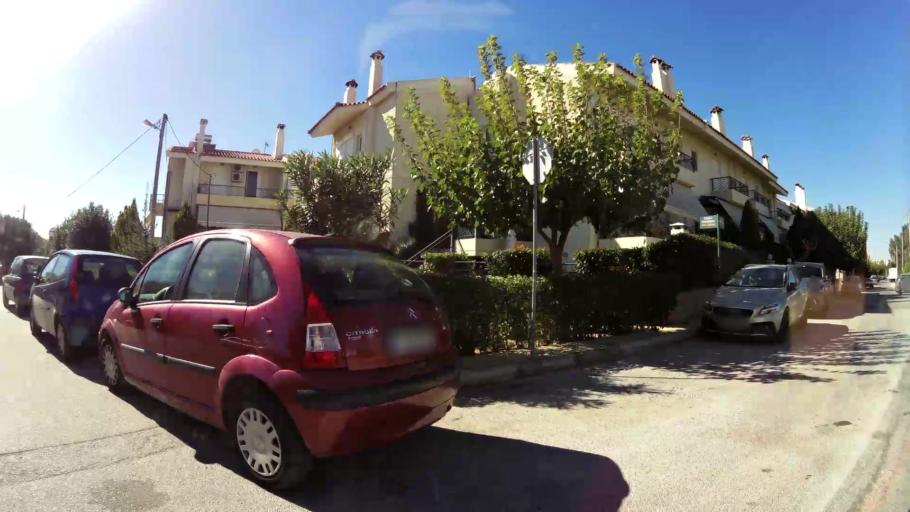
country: GR
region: Attica
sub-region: Nomarchia Anatolikis Attikis
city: Gerakas
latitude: 38.0049
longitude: 23.8606
